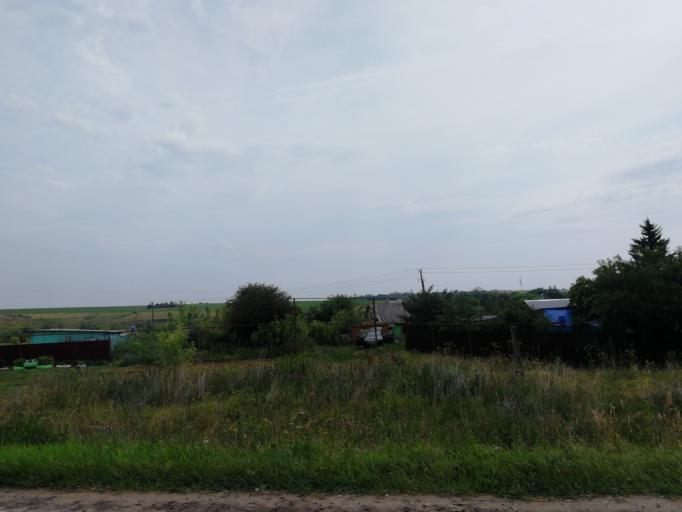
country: RU
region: Tula
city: Tovarkovskiy
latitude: 53.6984
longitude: 38.1653
